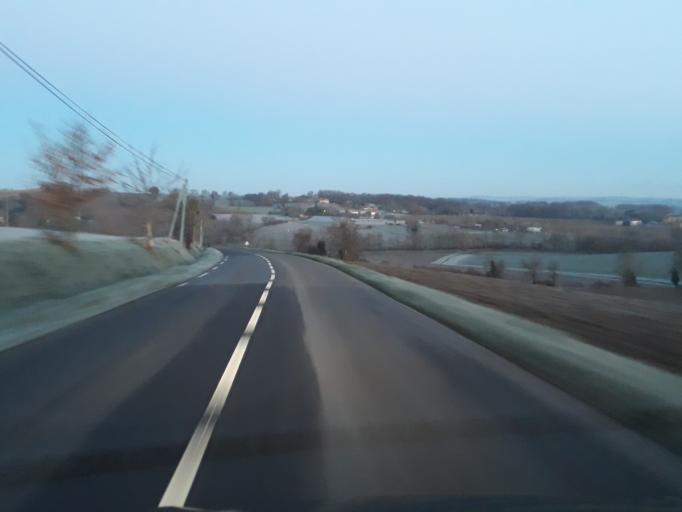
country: FR
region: Midi-Pyrenees
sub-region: Departement du Gers
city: Samatan
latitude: 43.4675
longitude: 0.9819
